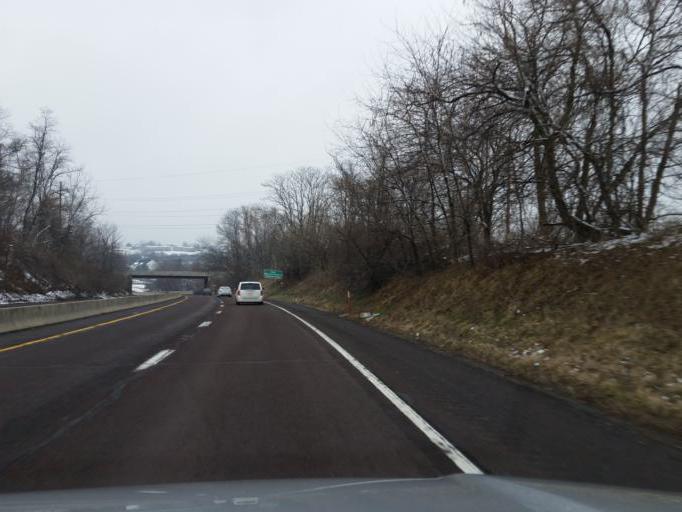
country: US
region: Pennsylvania
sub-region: Dauphin County
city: Hummelstown
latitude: 40.2608
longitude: -76.7223
